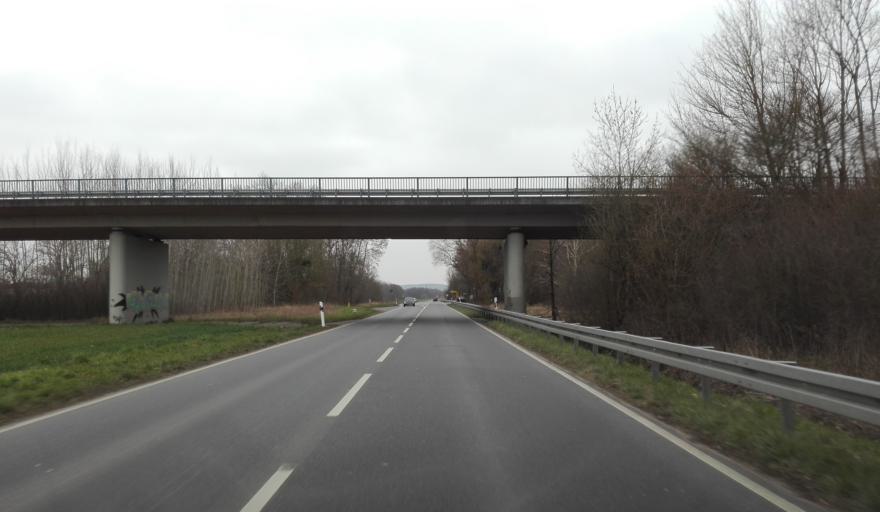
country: DE
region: Hesse
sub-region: Regierungsbezirk Darmstadt
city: Gross-Zimmern
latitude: 49.8844
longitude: 8.8140
